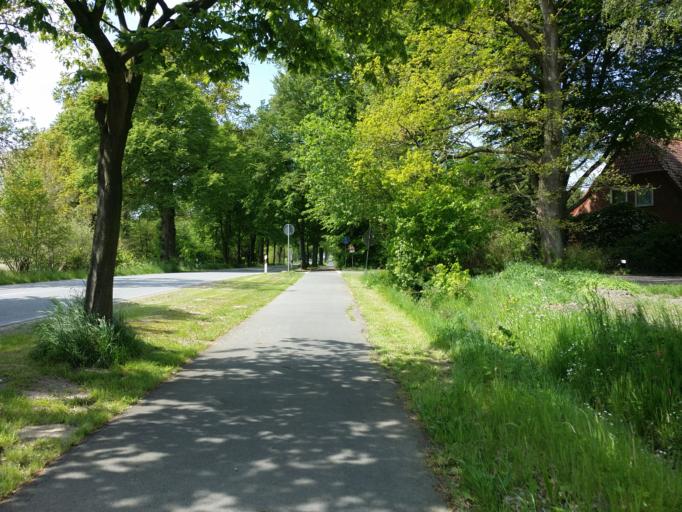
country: DE
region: Lower Saxony
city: Lubberstedt
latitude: 53.2968
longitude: 8.7828
